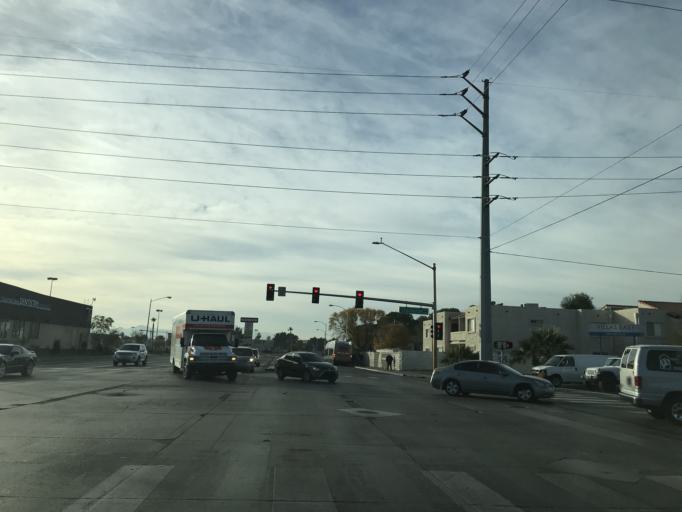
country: US
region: Nevada
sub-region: Clark County
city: Sunrise Manor
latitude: 36.1592
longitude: -115.0623
